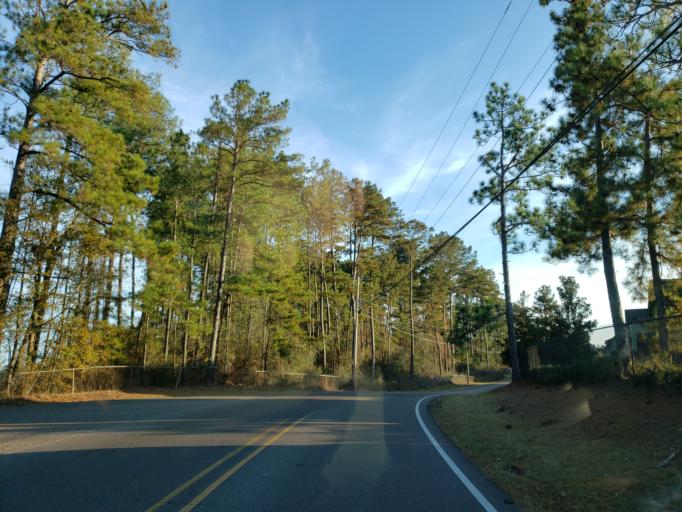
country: US
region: Mississippi
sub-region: Lamar County
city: Arnold Line
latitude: 31.3395
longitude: -89.3439
